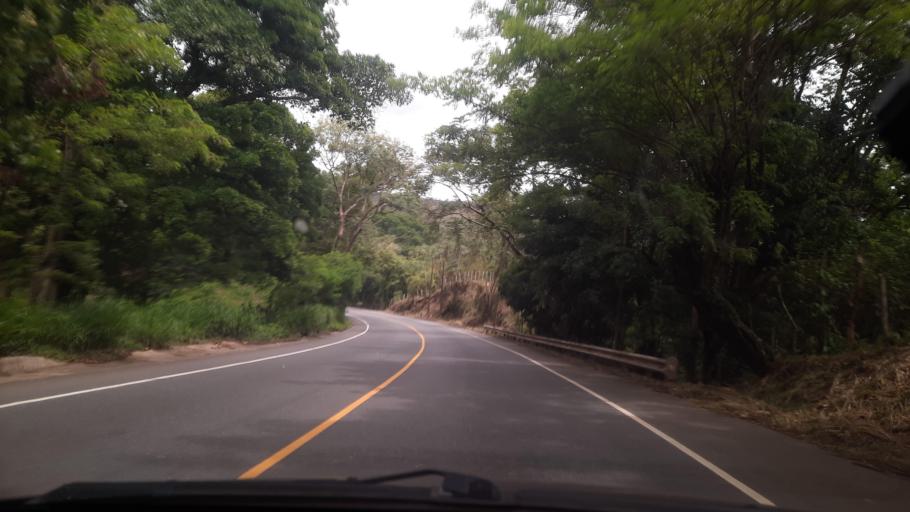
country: GT
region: Izabal
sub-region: Municipio de Los Amates
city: Los Amates
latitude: 15.2336
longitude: -89.1992
